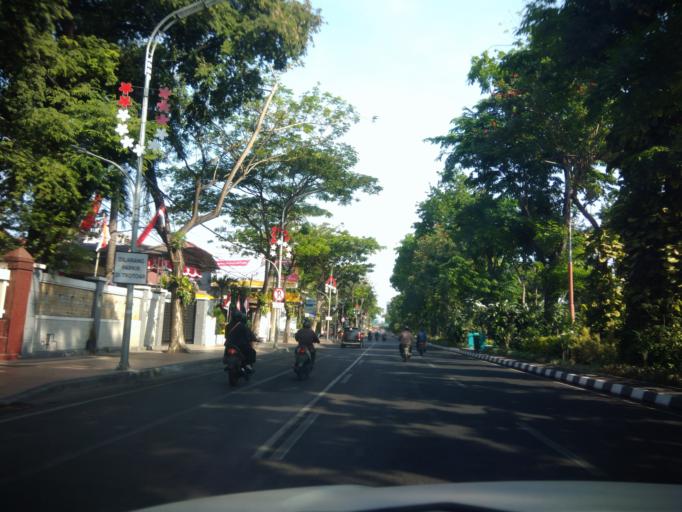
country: ID
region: East Java
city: Jagirsidosermo
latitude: -7.2919
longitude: 112.7391
